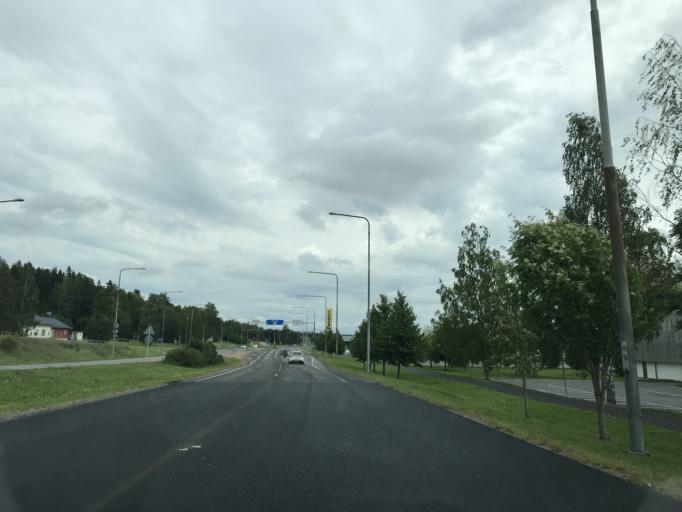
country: FI
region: Varsinais-Suomi
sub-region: Turku
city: Kaarina
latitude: 60.4090
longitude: 22.3670
